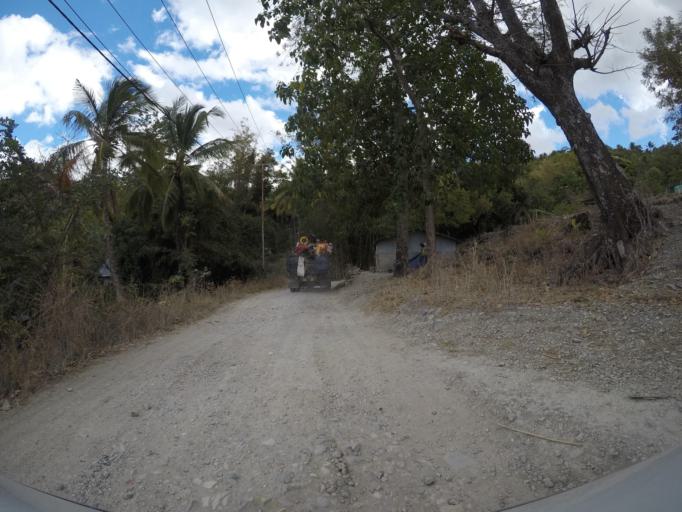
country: TL
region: Baucau
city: Baucau
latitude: -8.5118
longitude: 126.6809
